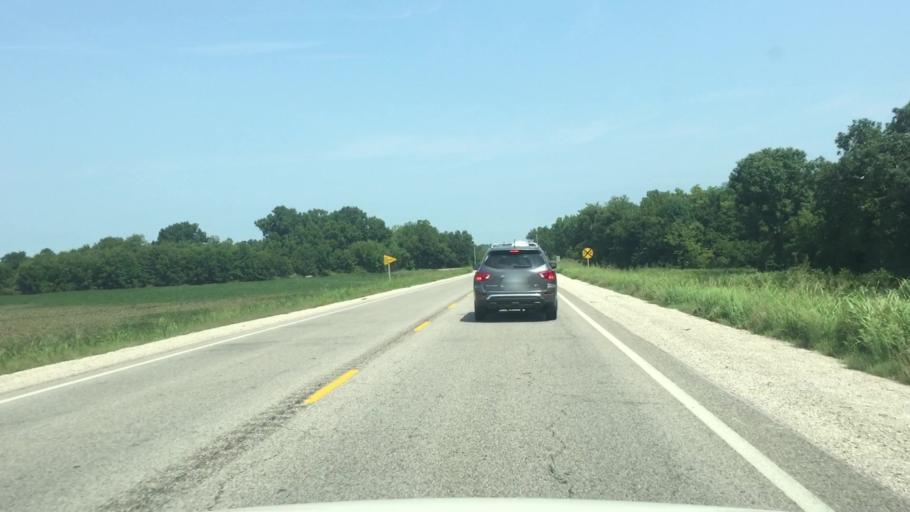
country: US
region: Kansas
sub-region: Montgomery County
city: Cherryvale
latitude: 37.1812
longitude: -95.5776
